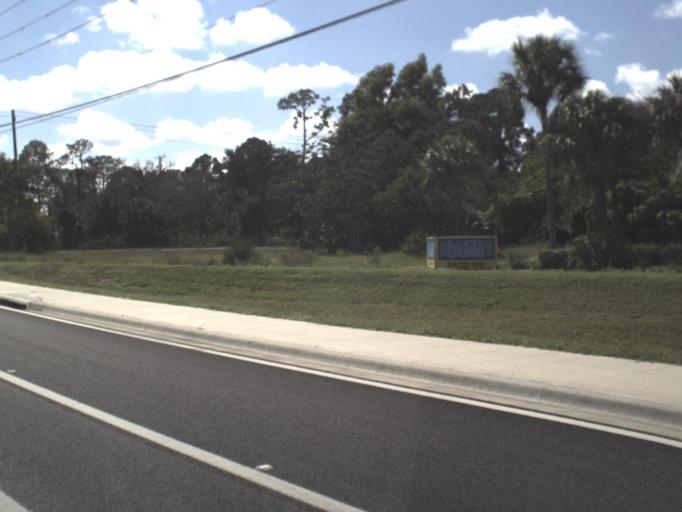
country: US
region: Florida
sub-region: Lee County
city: Estero
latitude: 26.4429
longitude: -81.8115
